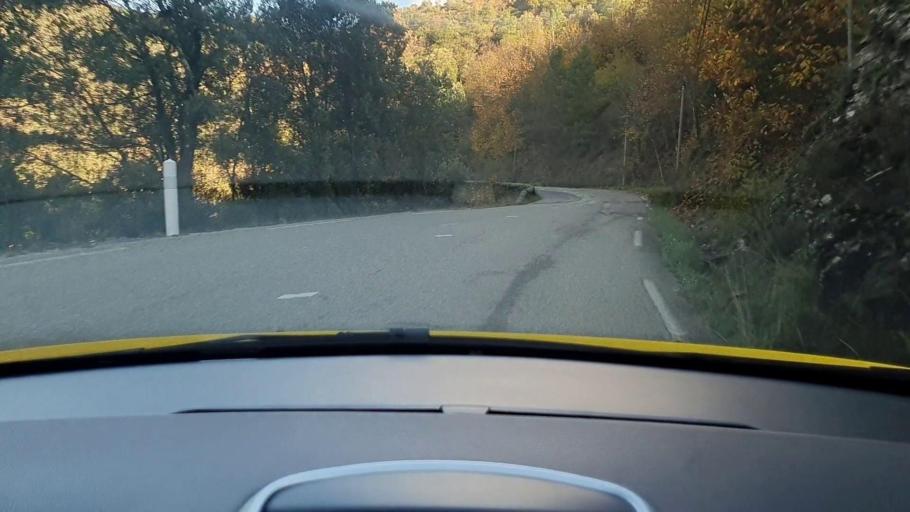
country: FR
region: Languedoc-Roussillon
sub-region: Departement du Gard
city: Valleraugue
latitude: 44.1230
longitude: 3.7374
